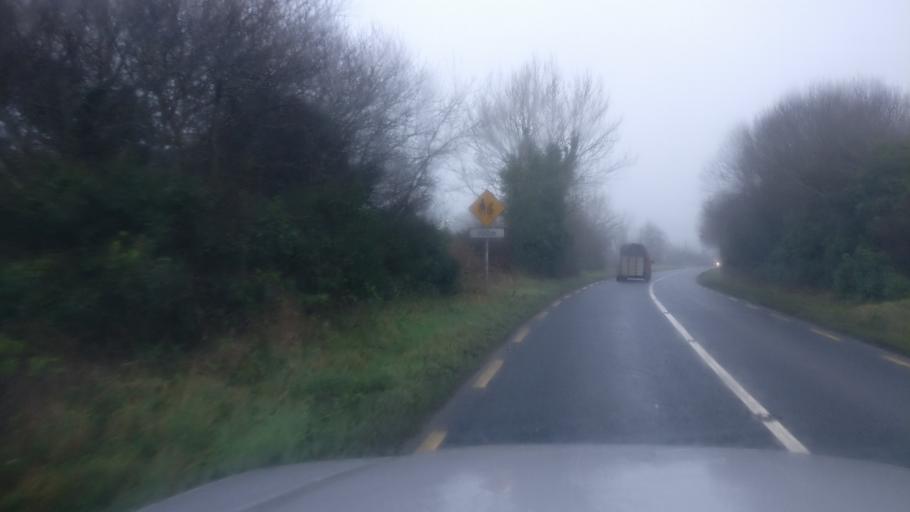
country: IE
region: Connaught
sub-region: County Galway
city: Loughrea
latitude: 53.1656
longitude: -8.6768
